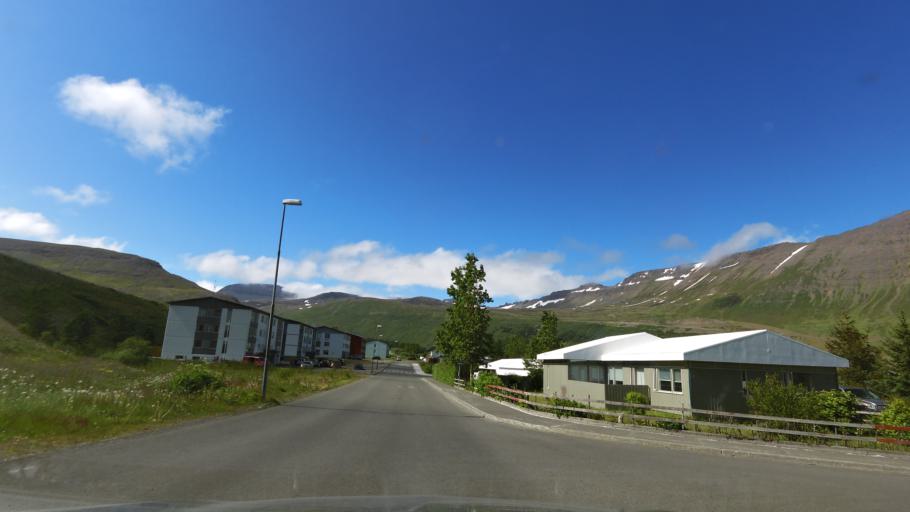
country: IS
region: Westfjords
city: Isafjoerdur
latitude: 66.0545
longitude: -23.1738
